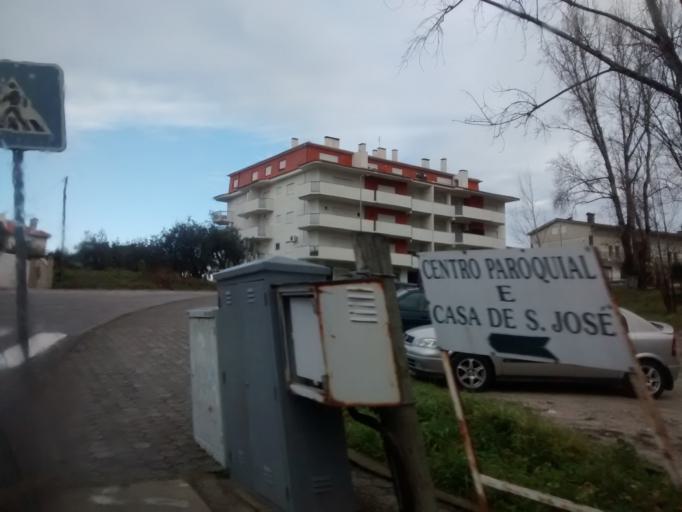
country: PT
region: Guarda
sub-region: Seia
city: Seia
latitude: 40.4137
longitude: -7.7070
